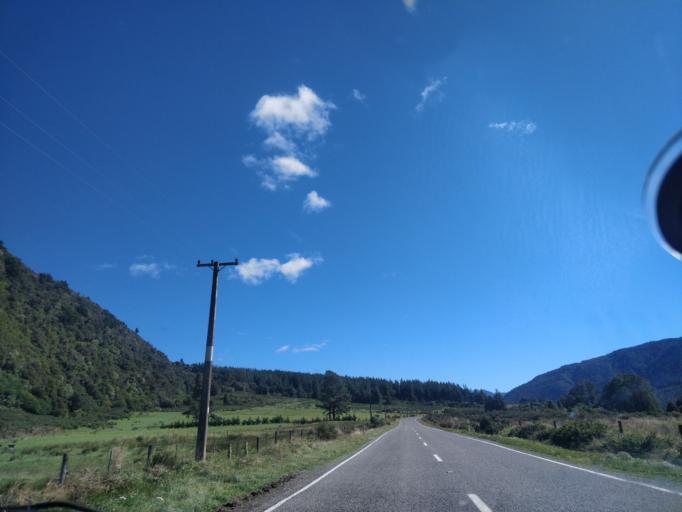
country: NZ
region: West Coast
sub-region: Grey District
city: Greymouth
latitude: -42.7554
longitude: 171.5489
